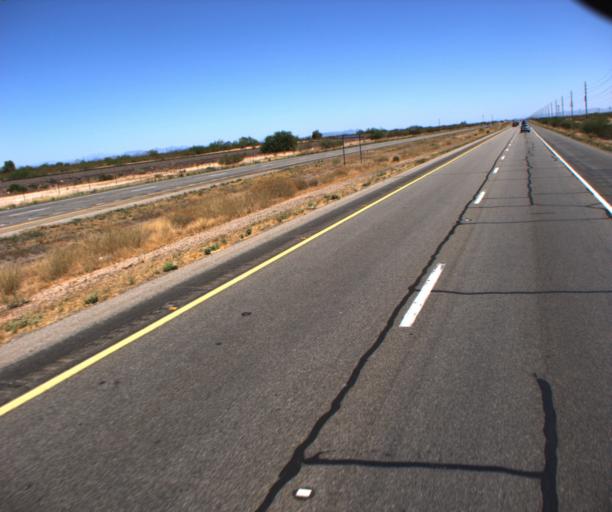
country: US
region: Arizona
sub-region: Maricopa County
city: Sun City West
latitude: 33.7608
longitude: -112.5069
